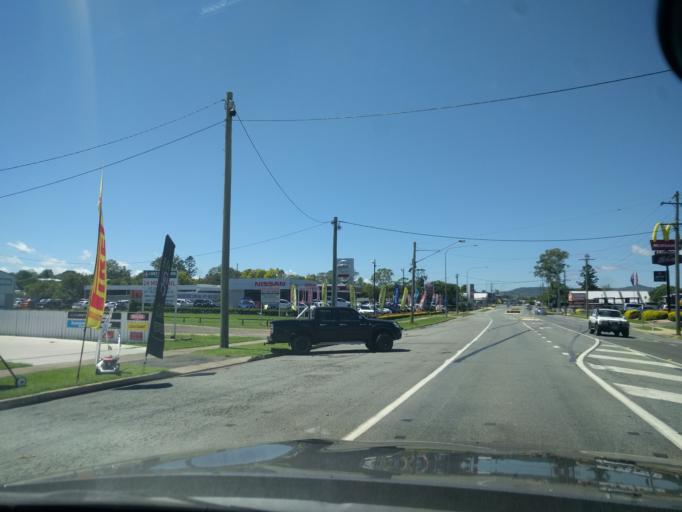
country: AU
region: Queensland
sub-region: Logan
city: Cedar Vale
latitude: -27.9814
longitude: 152.9948
